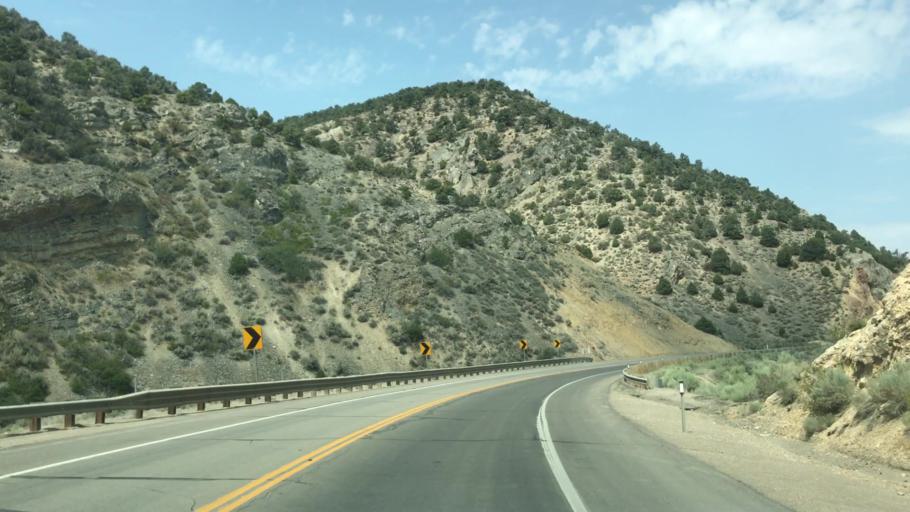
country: US
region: Nevada
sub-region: White Pine County
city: Ely
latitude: 39.2465
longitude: -114.9050
